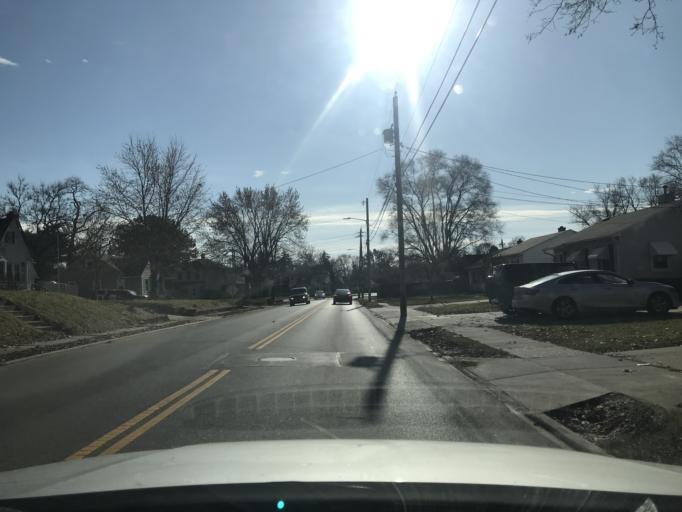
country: US
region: Iowa
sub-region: Scott County
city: Davenport
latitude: 41.5240
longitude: -90.6150
